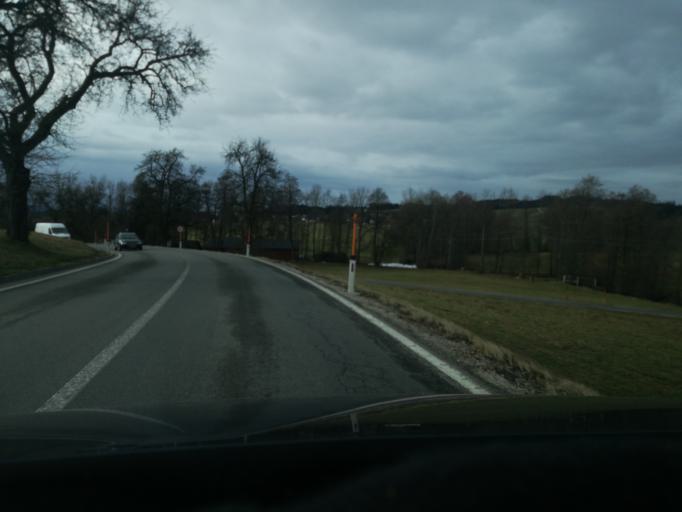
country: AT
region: Upper Austria
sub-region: Politischer Bezirk Vocklabruck
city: Frankenburg
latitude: 48.0845
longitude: 13.4822
